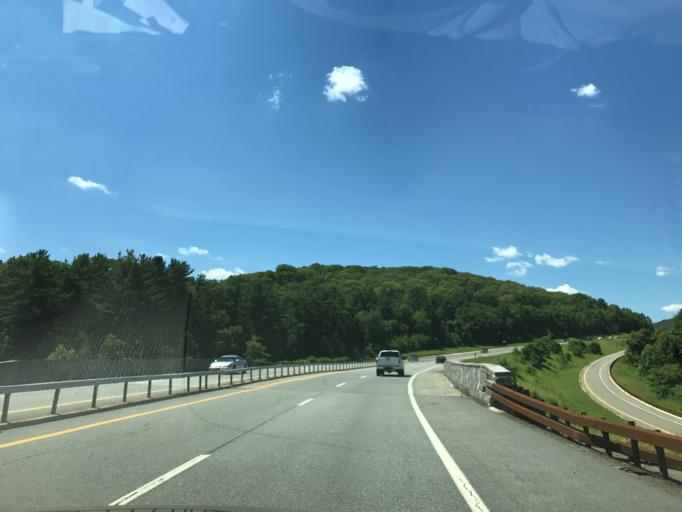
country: US
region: New York
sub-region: Dutchess County
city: Brinckerhoff
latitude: 41.5131
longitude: -73.7876
